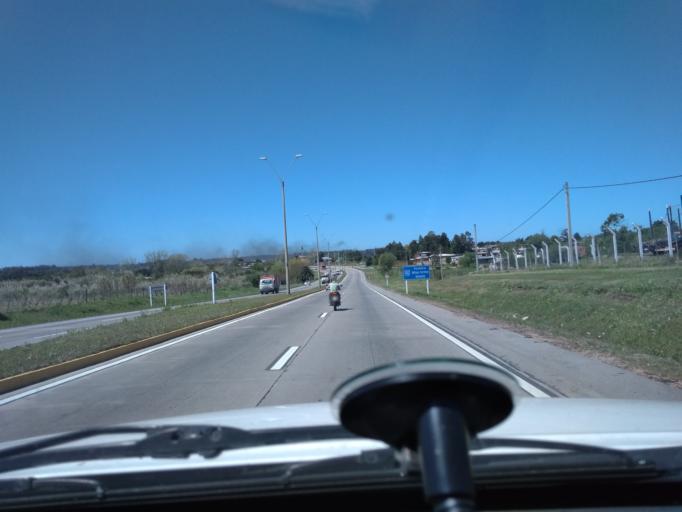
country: UY
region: Canelones
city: Toledo
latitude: -34.7945
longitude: -56.1221
